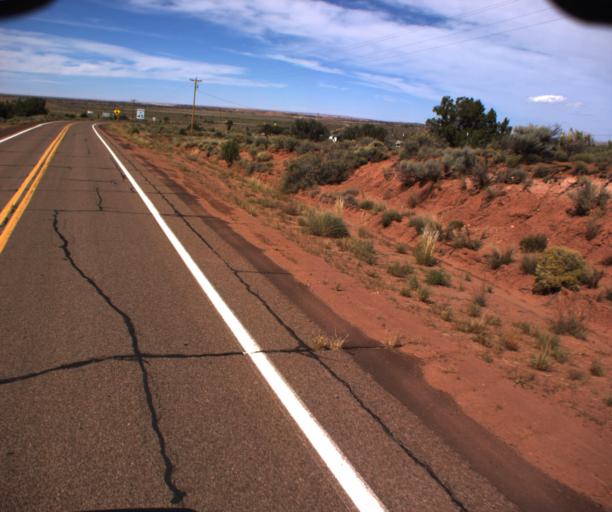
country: US
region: Arizona
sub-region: Apache County
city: Saint Johns
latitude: 34.6168
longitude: -109.6615
